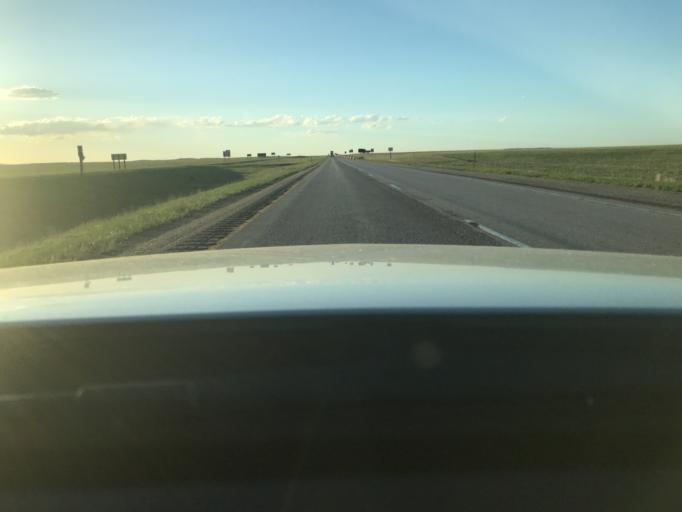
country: US
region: Wyoming
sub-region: Platte County
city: Wheatland
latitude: 42.2437
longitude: -105.0291
